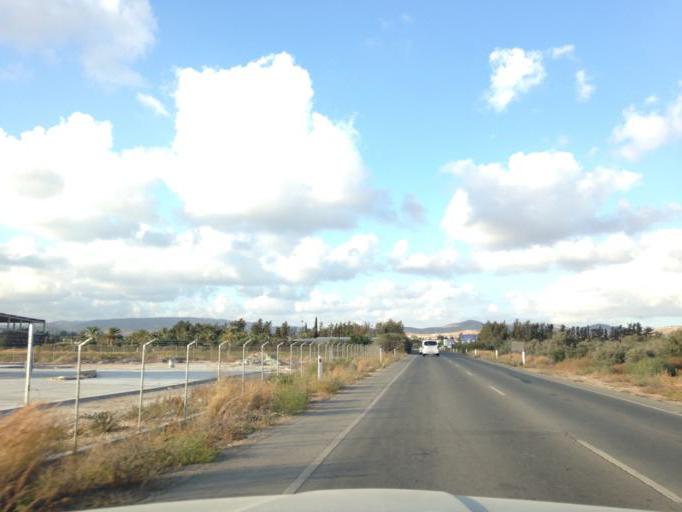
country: CY
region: Pafos
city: Paphos
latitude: 34.7219
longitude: 32.5147
